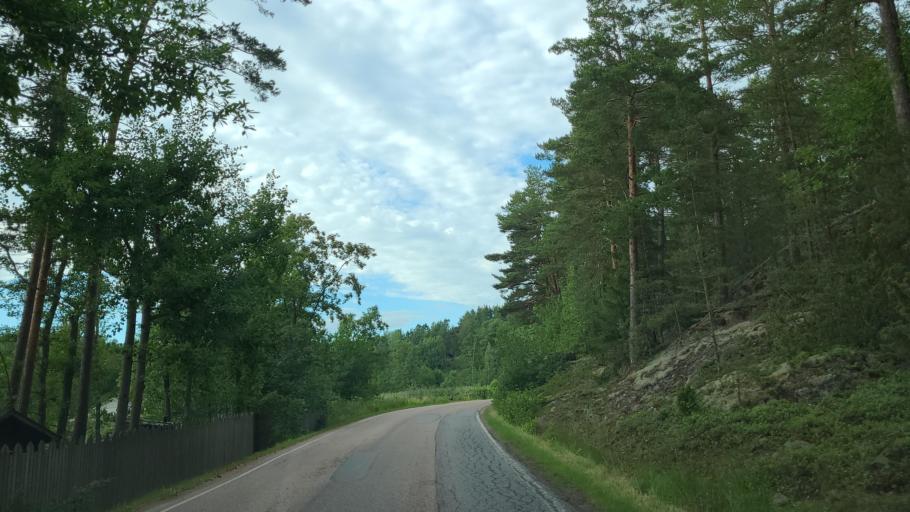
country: FI
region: Varsinais-Suomi
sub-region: Turku
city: Rymaettylae
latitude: 60.3421
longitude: 21.9779
